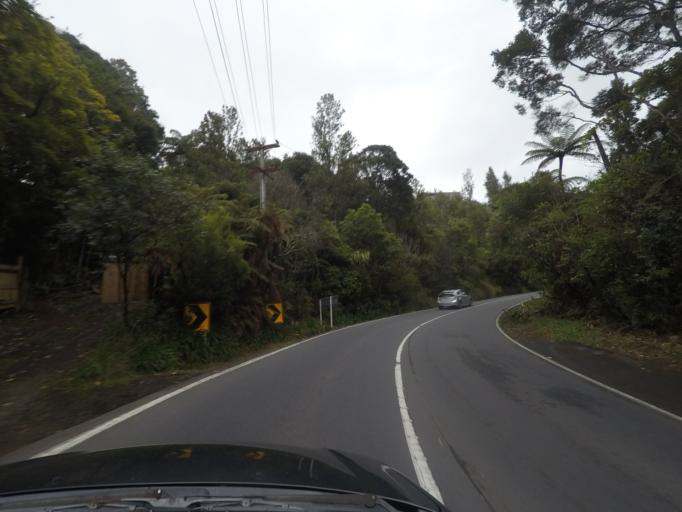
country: NZ
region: Auckland
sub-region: Auckland
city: Titirangi
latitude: -36.9333
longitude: 174.5809
